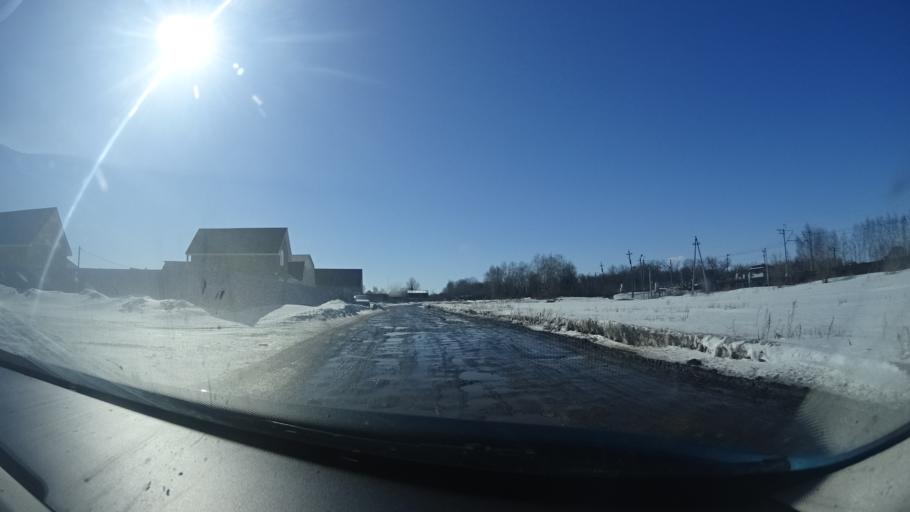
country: RU
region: Bashkortostan
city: Chishmy
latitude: 54.5789
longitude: 55.3725
